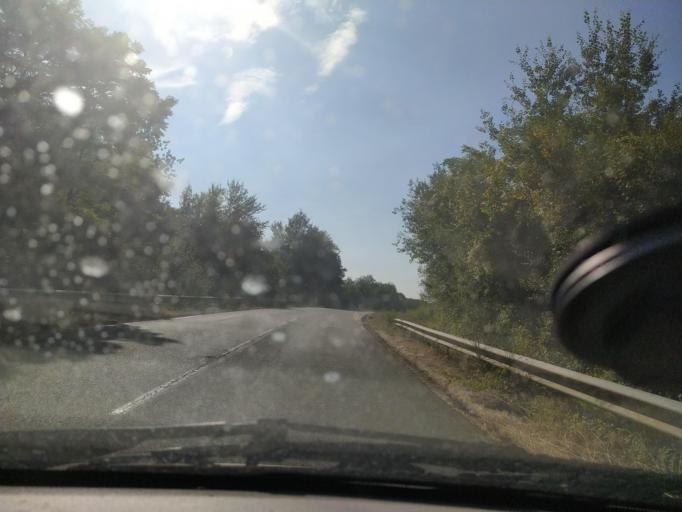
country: FR
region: Midi-Pyrenees
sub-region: Departement du Gers
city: Nogaro
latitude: 43.7882
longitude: 0.0074
